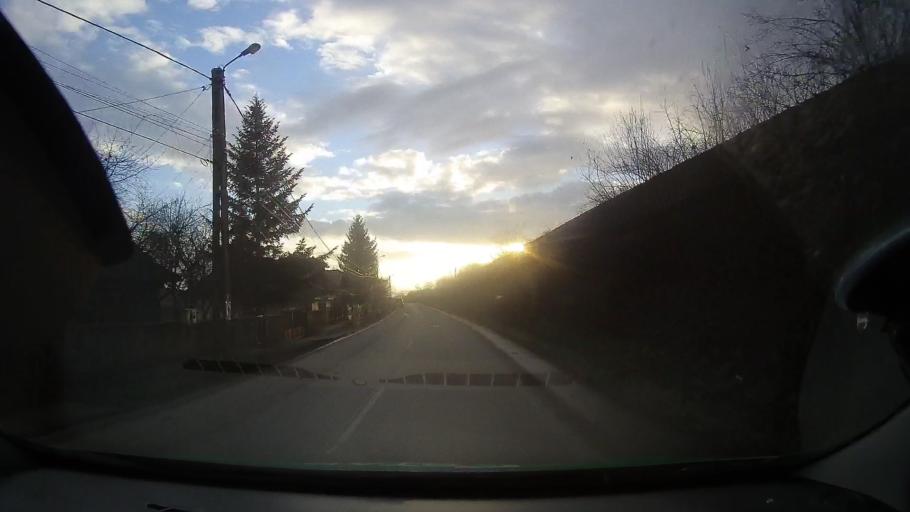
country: RO
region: Alba
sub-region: Oras Ocna Mures
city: Razboieni-Cetate
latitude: 46.4209
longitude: 23.8774
